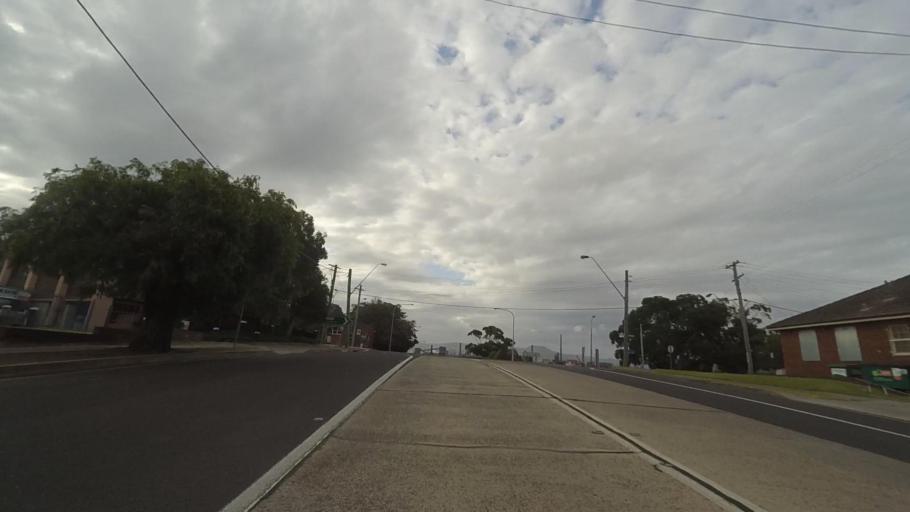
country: AU
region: New South Wales
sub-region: Wollongong
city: Port Kembla
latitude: -34.4799
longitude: 150.9020
